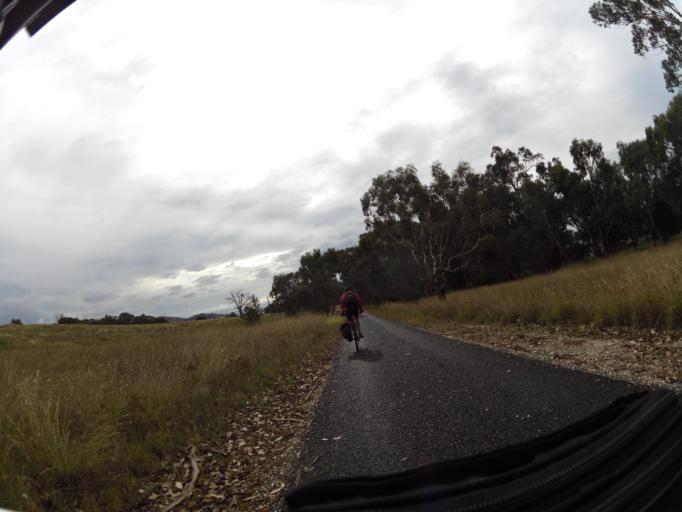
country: AU
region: New South Wales
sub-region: Albury Municipality
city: East Albury
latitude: -36.1421
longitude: 146.9953
